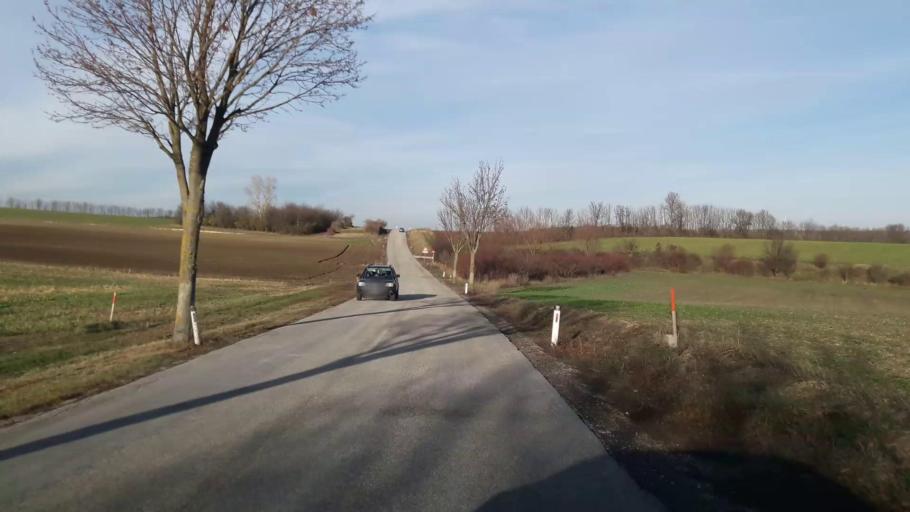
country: AT
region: Lower Austria
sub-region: Politischer Bezirk Ganserndorf
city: Gross-Schweinbarth
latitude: 48.3996
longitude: 16.6337
